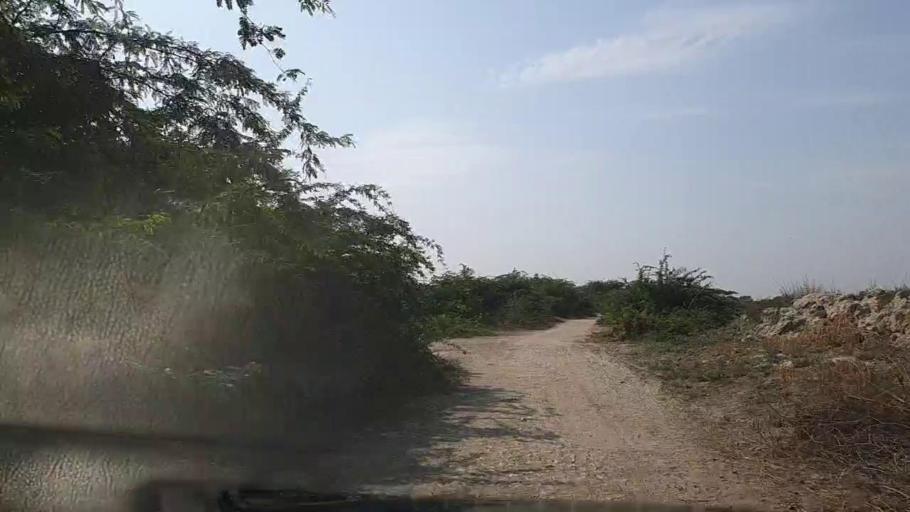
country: PK
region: Sindh
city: Thatta
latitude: 24.7716
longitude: 67.8188
